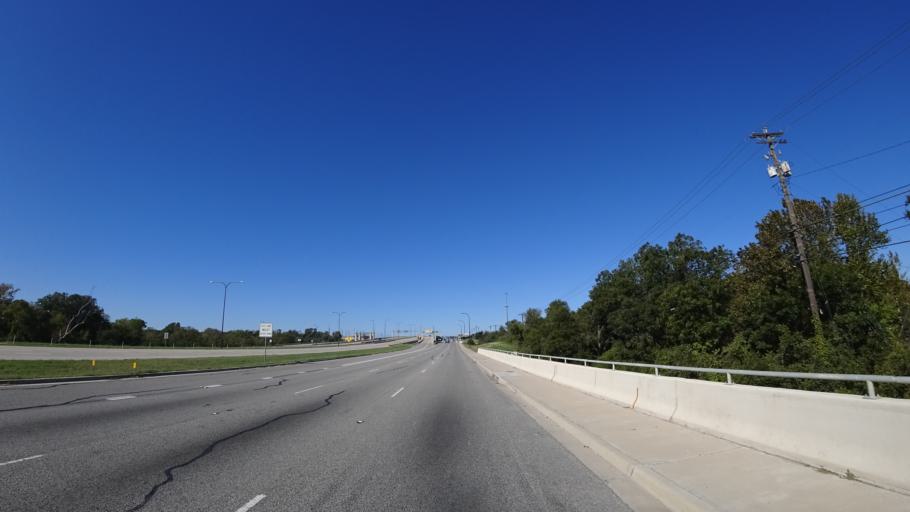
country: US
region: Texas
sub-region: Travis County
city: Manor
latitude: 30.3294
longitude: -97.6490
